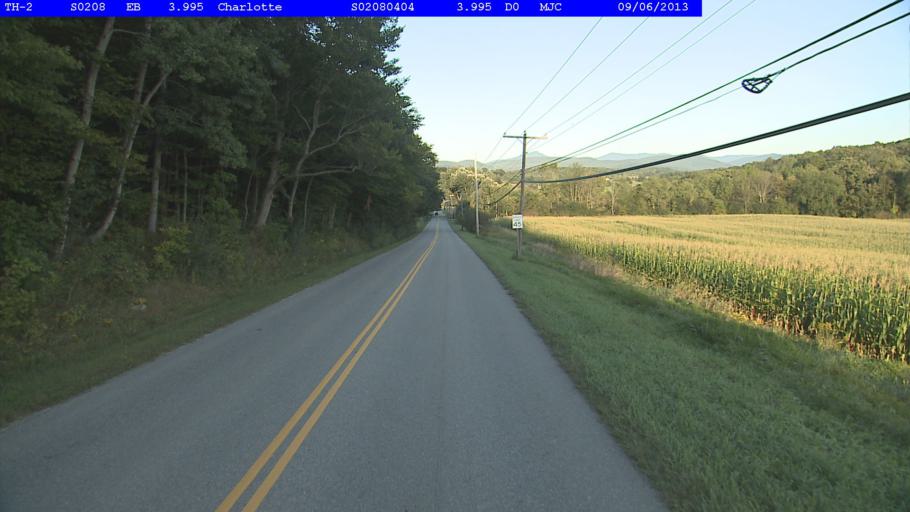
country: US
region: Vermont
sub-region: Chittenden County
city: Hinesburg
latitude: 44.3221
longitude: -73.1687
